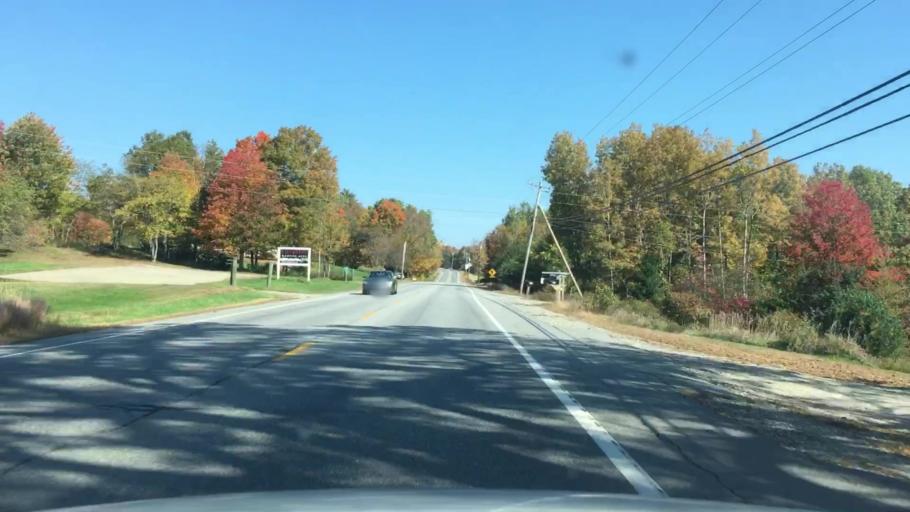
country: US
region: Maine
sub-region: Sagadahoc County
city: Topsham
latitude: 43.9854
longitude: -69.9573
